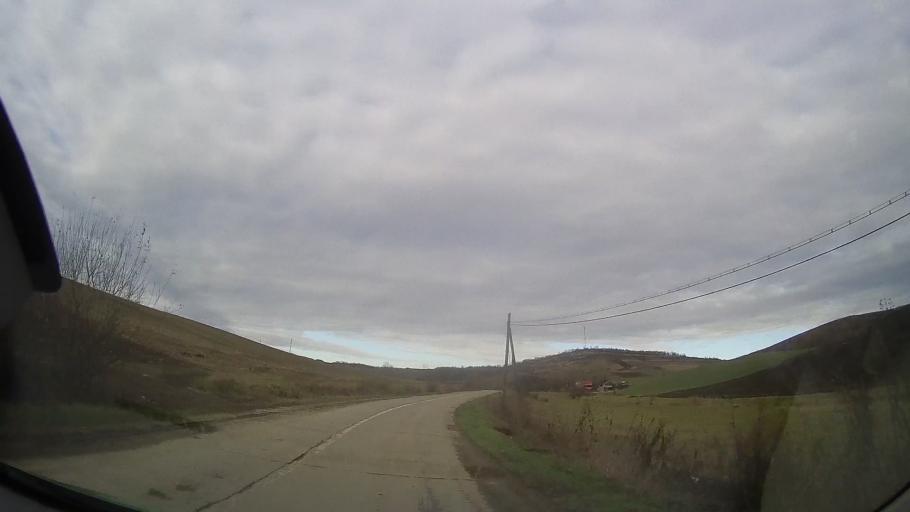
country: RO
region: Bistrita-Nasaud
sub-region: Comuna Micestii de Campie
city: Micestii de Campie
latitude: 46.8422
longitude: 24.3014
